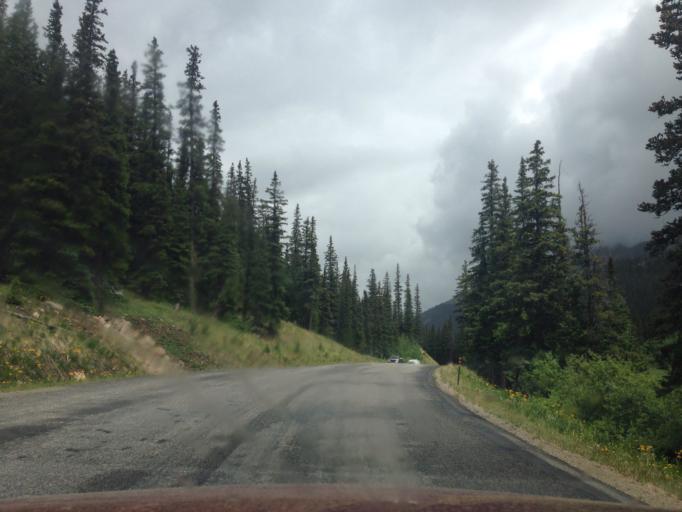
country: US
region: Colorado
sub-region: Clear Creek County
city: Georgetown
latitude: 39.6224
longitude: -105.7137
